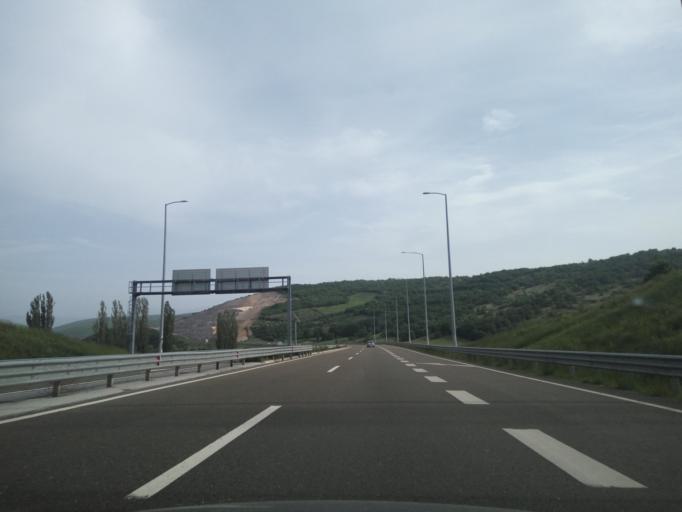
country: XK
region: Prizren
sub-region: Komuna e Therandes
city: Nishor
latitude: 42.4620
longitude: 20.8064
